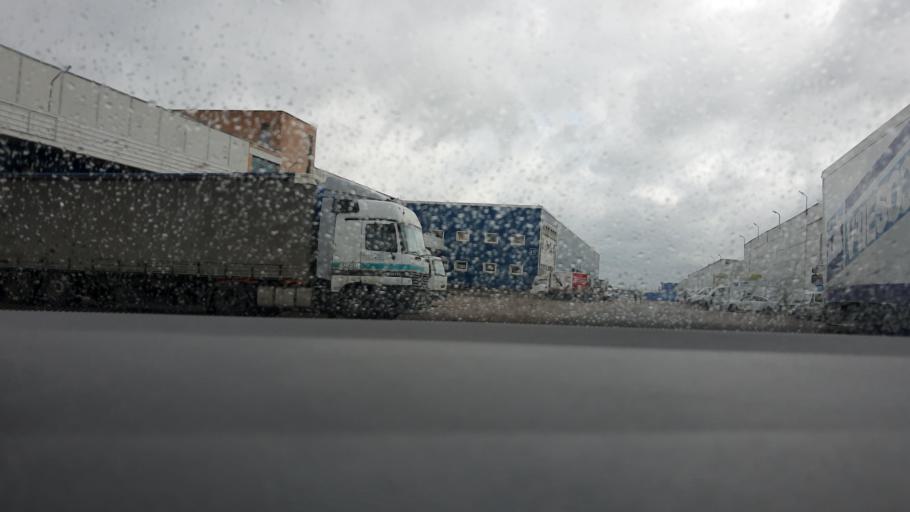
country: RU
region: Moskovskaya
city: Biryulevo Zapadnoye
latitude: 55.5921
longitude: 37.6219
